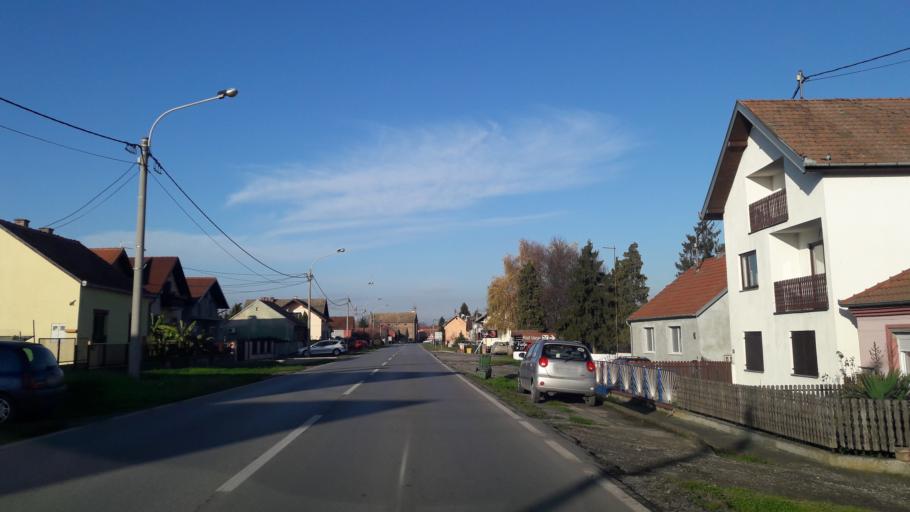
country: HR
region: Osjecko-Baranjska
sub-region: Grad Osijek
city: Bilje
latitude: 45.5969
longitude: 18.7426
